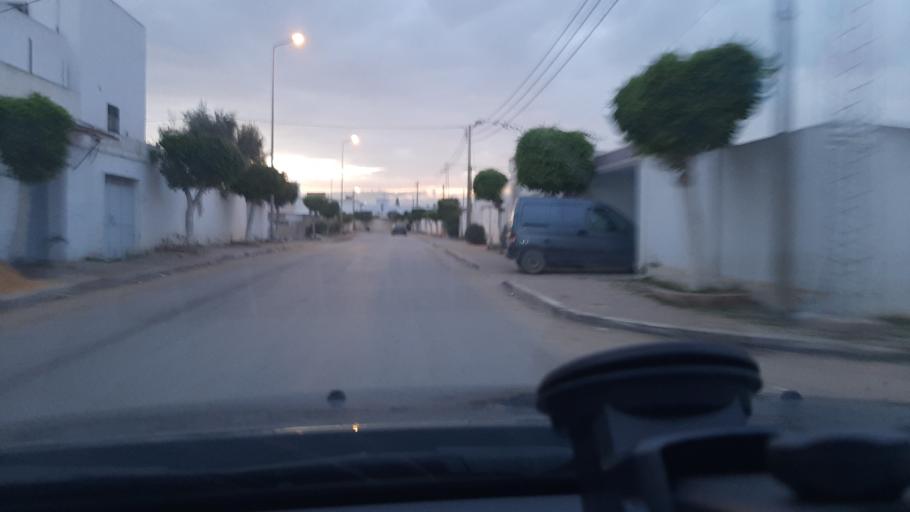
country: TN
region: Safaqis
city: Sfax
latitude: 34.7663
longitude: 10.6999
